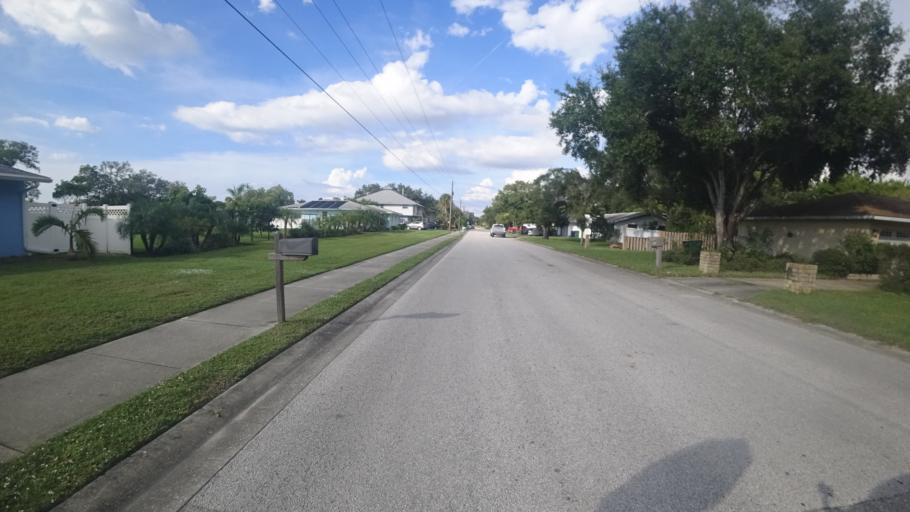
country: US
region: Florida
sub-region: Manatee County
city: Palmetto
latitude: 27.5190
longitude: -82.5893
